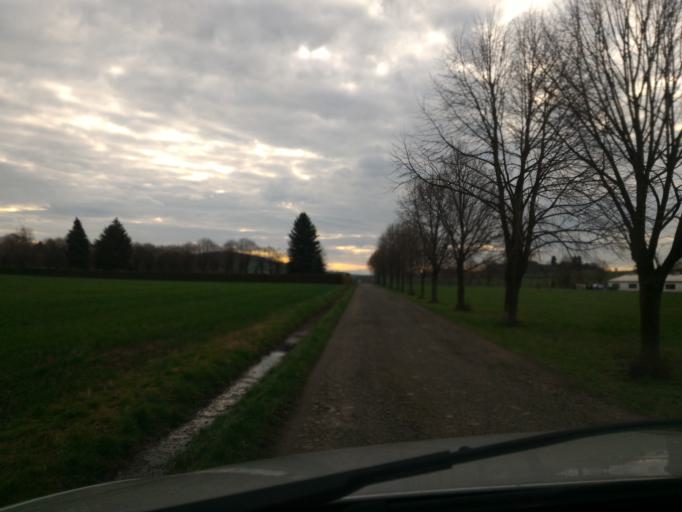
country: DE
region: Saxony
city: Leutersdorf
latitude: 50.9620
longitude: 14.6528
